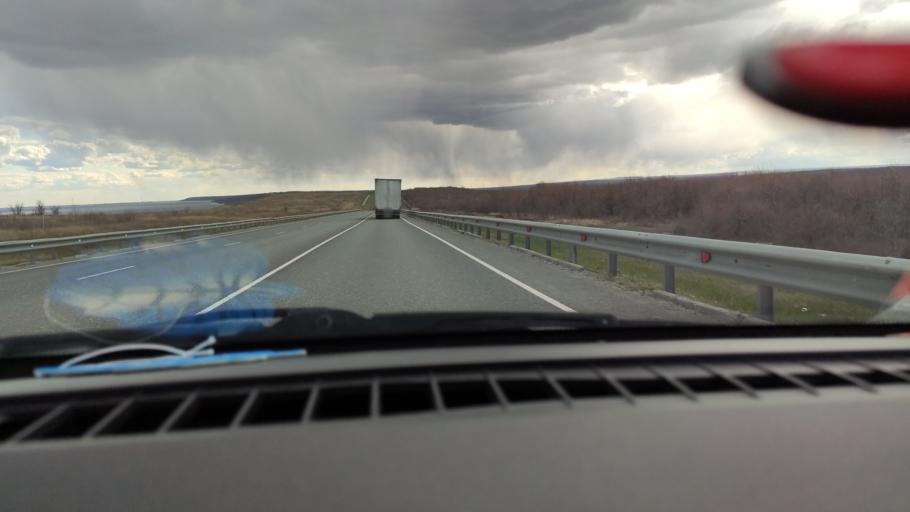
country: RU
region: Saratov
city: Alekseyevka
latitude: 52.2133
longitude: 47.8847
